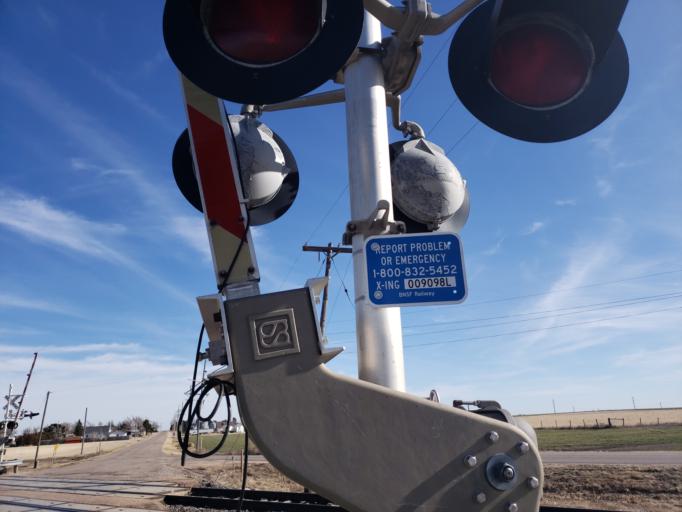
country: US
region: Kansas
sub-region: Ford County
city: Dodge City
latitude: 37.7789
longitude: -99.8985
